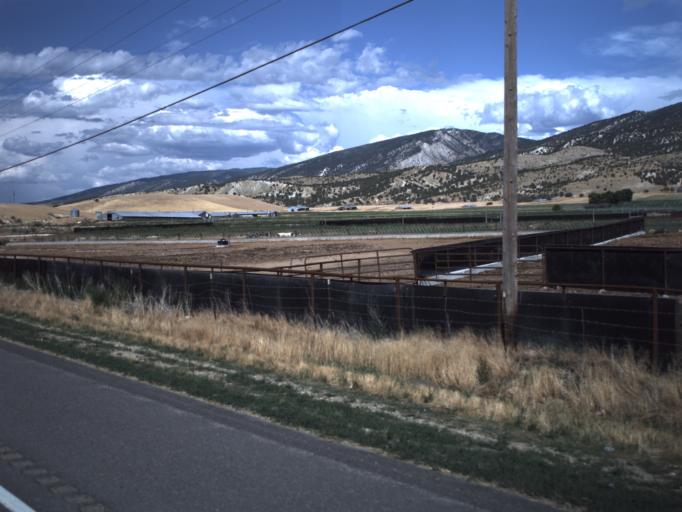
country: US
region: Utah
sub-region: Sanpete County
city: Manti
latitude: 39.2948
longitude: -111.6217
